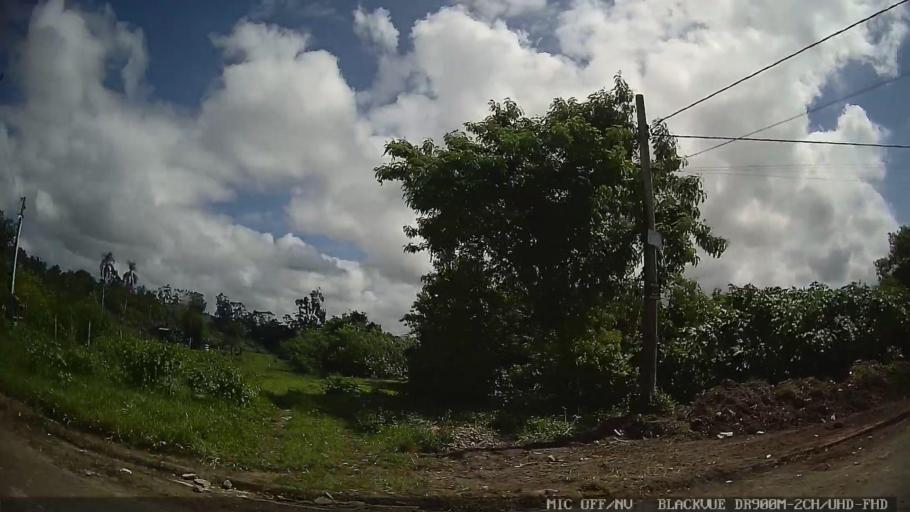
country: BR
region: Sao Paulo
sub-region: Peruibe
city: Peruibe
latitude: -24.3063
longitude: -47.0080
